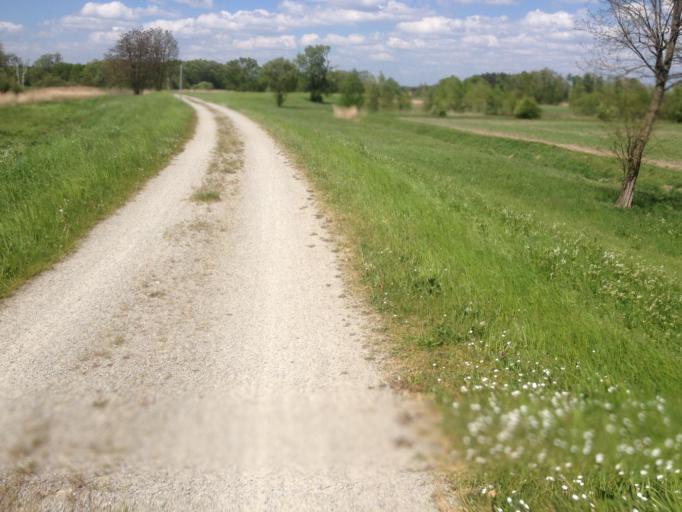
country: DE
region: Brandenburg
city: Drehnow
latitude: 51.8410
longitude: 14.3400
